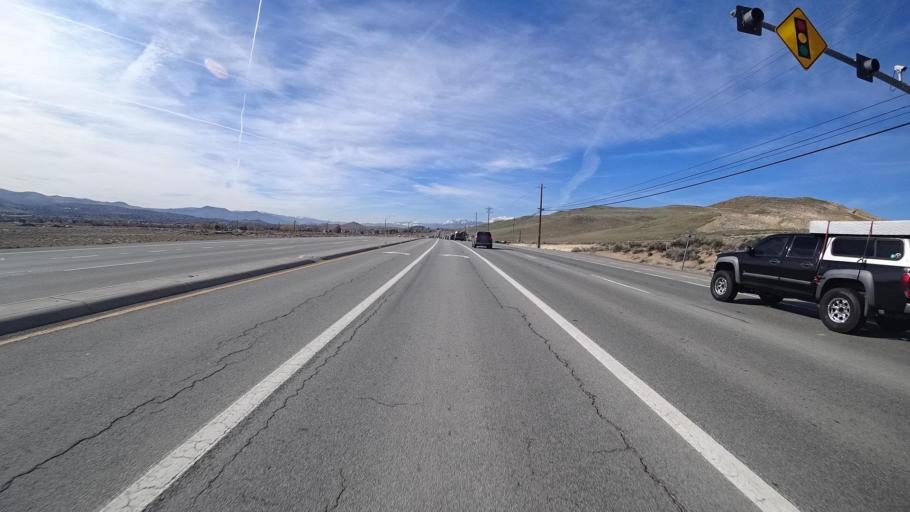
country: US
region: Nevada
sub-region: Washoe County
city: Spanish Springs
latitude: 39.6105
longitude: -119.7310
